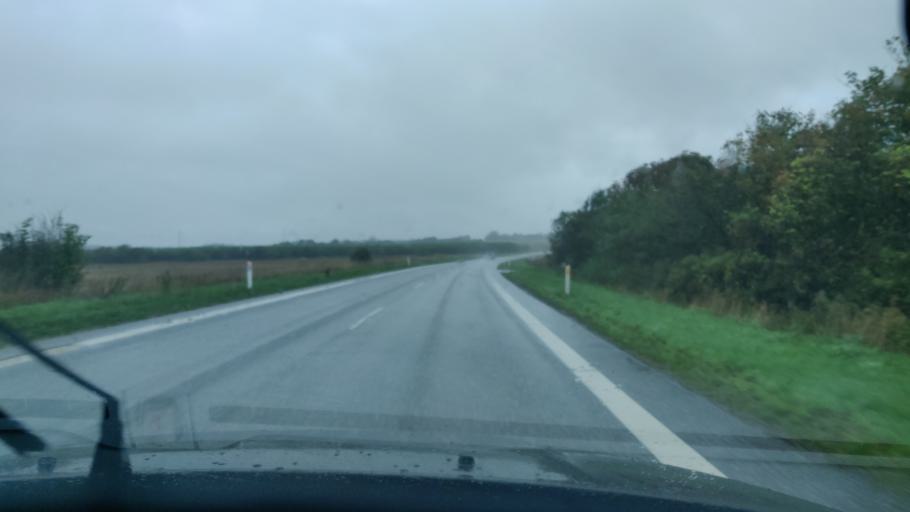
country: DK
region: North Denmark
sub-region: Thisted Kommune
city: Hurup
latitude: 56.8528
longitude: 8.5415
